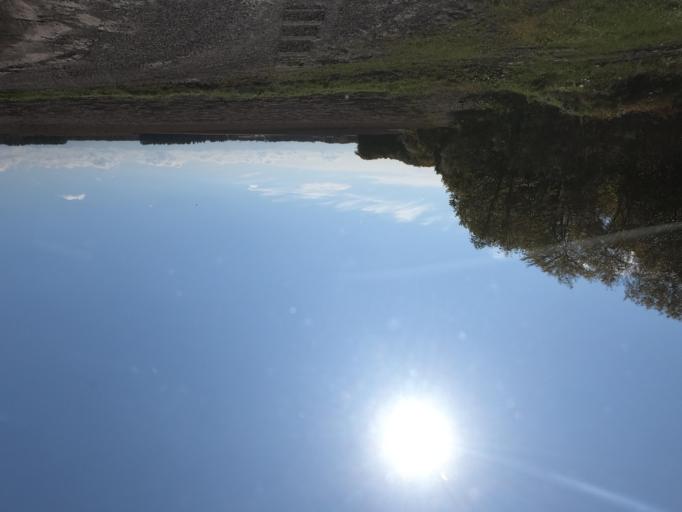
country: JP
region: Hokkaido
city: Otofuke
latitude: 43.2355
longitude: 143.2608
